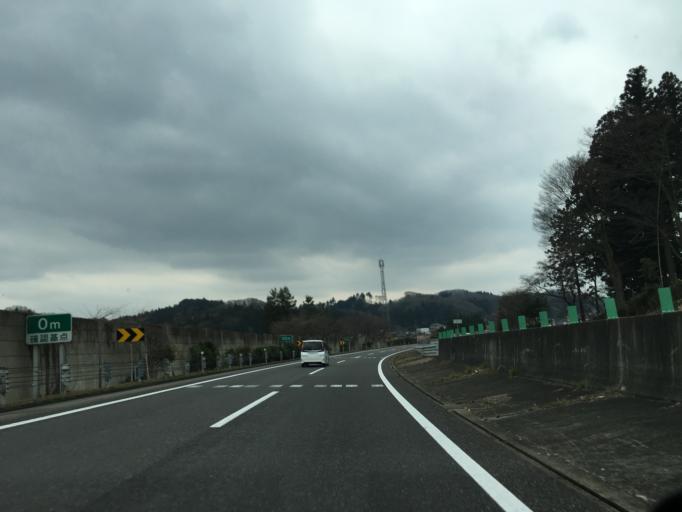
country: JP
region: Fukushima
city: Sukagawa
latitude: 37.1636
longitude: 140.2684
